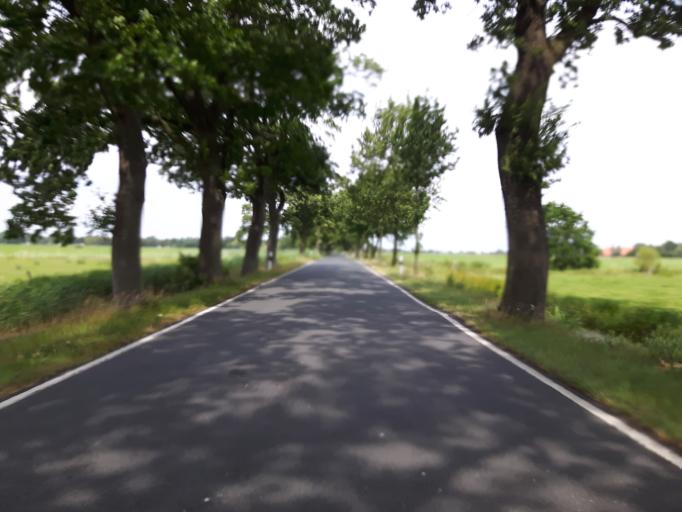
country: DE
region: Lower Saxony
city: Rastede
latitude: 53.3345
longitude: 8.2540
